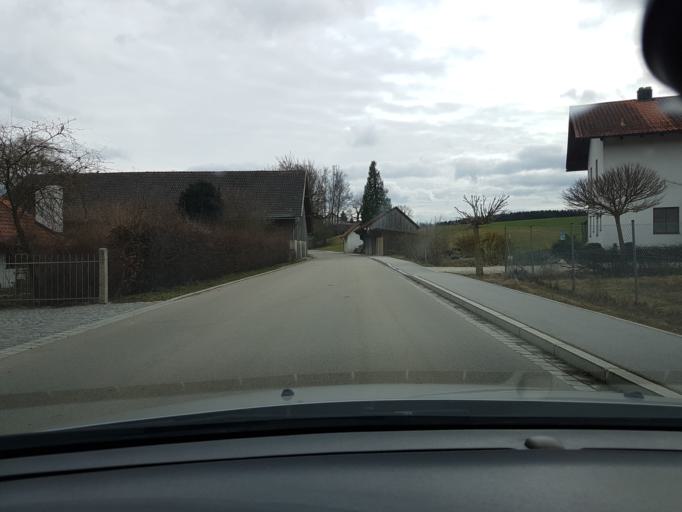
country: DE
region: Bavaria
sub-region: Lower Bavaria
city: Eging
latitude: 48.4952
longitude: 12.2097
